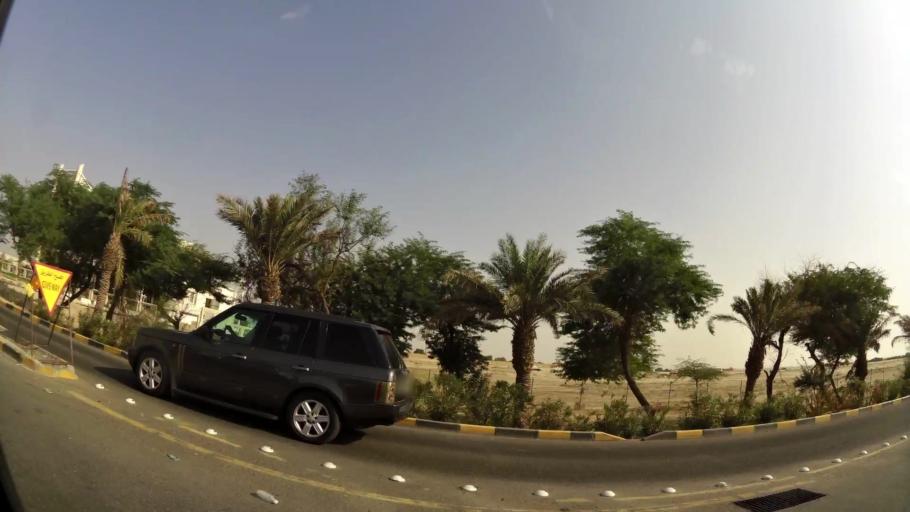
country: KW
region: Muhafazat al Jahra'
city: Al Jahra'
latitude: 29.3376
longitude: 47.7110
